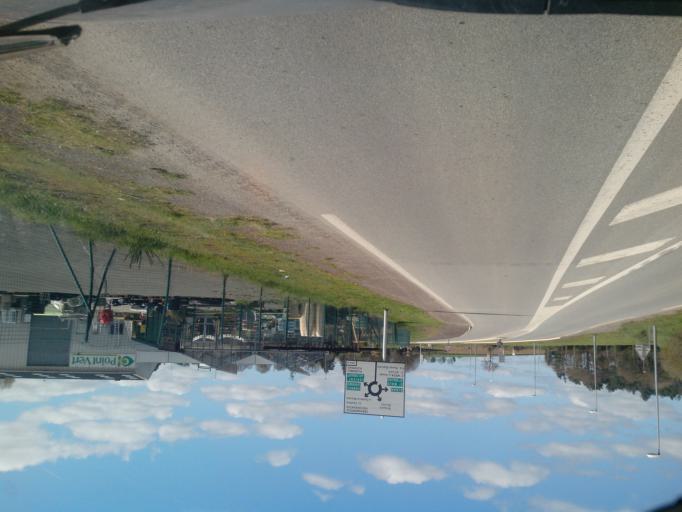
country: FR
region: Brittany
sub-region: Departement du Morbihan
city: Mauron
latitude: 48.0735
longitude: -2.2822
